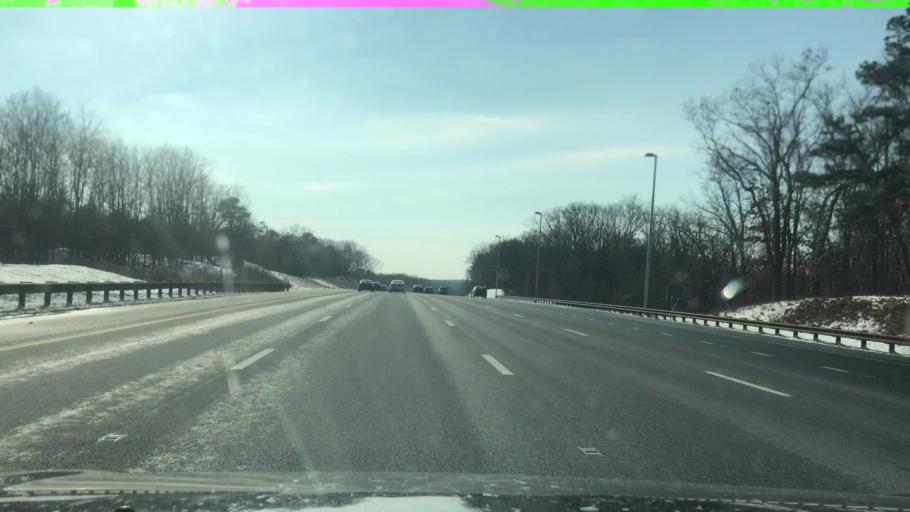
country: US
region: New Jersey
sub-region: Monmouth County
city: Ramtown
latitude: 40.1559
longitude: -74.1046
